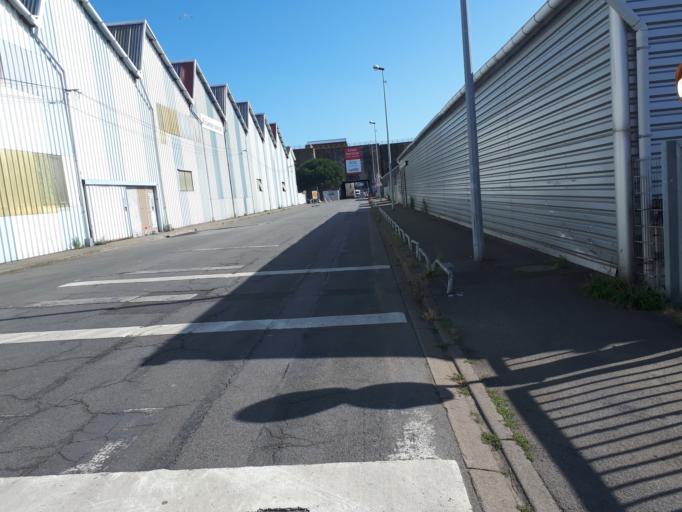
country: FR
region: Pays de la Loire
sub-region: Departement de la Loire-Atlantique
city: Saint-Nazaire
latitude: 47.2769
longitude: -2.1990
